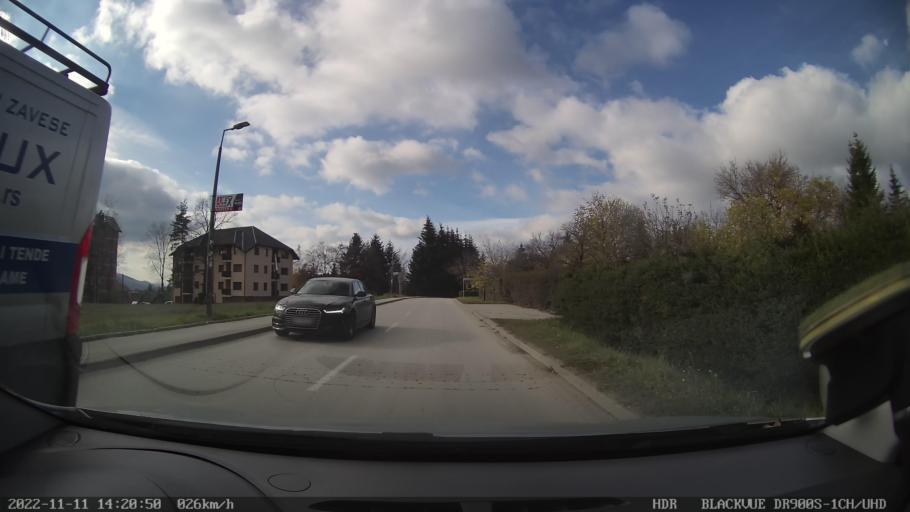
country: RS
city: Zlatibor
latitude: 43.7373
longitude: 19.7065
